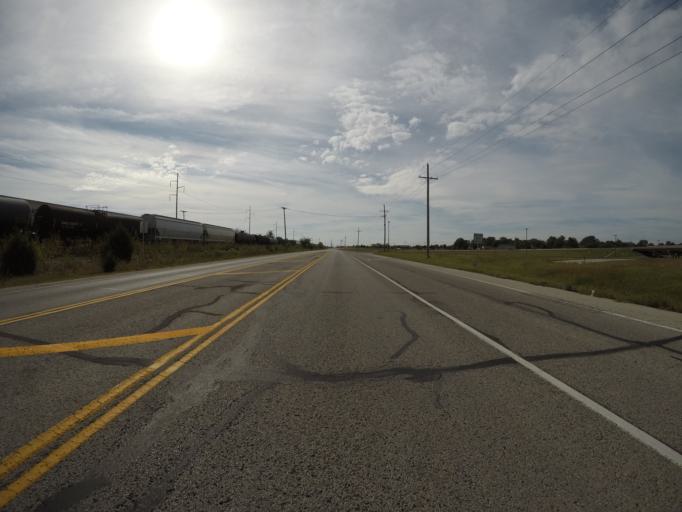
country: US
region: Kansas
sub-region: Johnson County
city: Gardner
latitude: 38.8133
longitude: -94.8988
